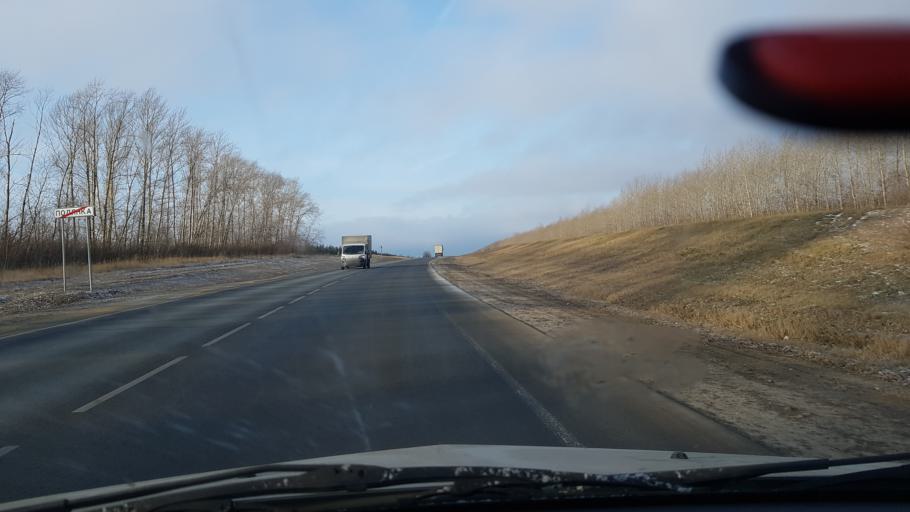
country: RU
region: Tatarstan
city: Laishevo
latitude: 55.3917
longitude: 49.7913
